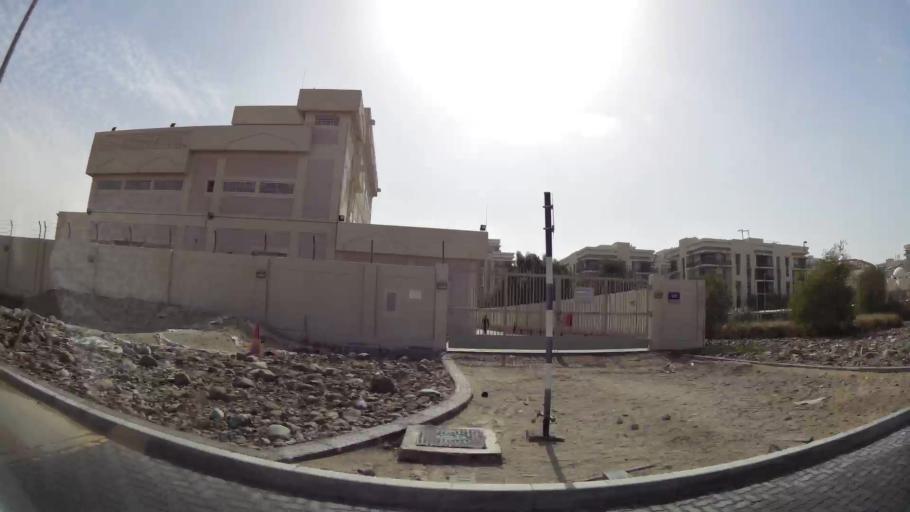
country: AE
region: Abu Dhabi
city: Abu Dhabi
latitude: 24.4119
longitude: 54.5383
